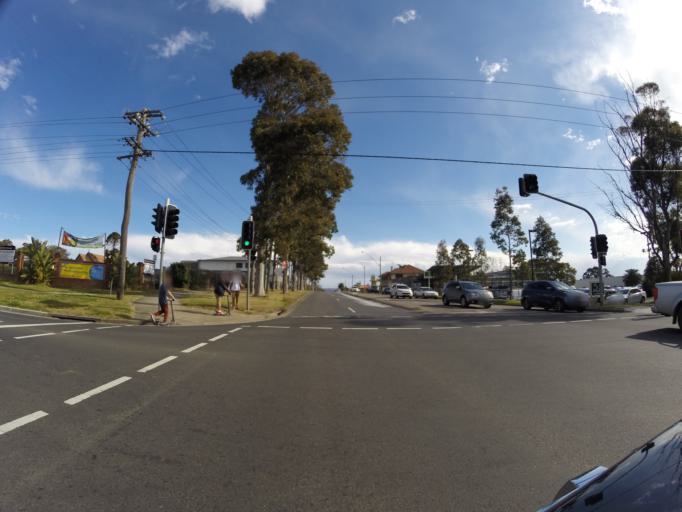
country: AU
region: New South Wales
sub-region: Camden
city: Narellan
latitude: -34.0416
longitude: 150.7323
